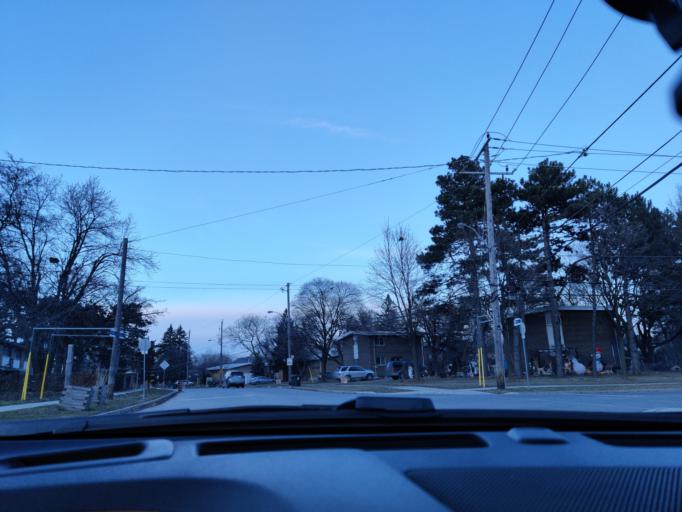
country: CA
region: Ontario
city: Toronto
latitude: 43.7200
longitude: -79.4411
